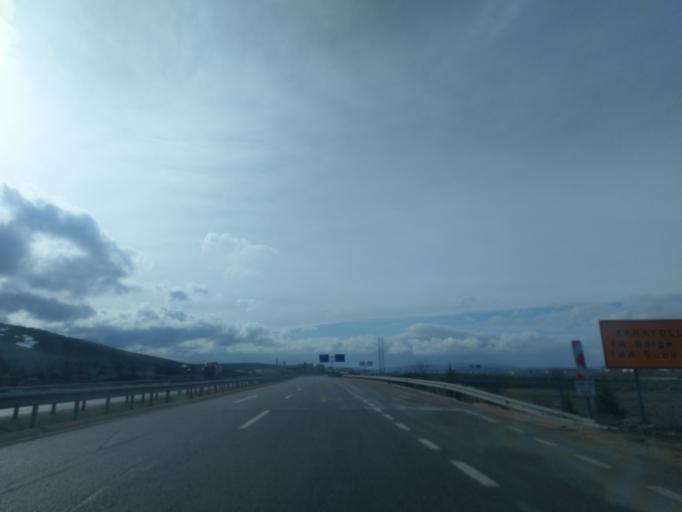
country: TR
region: Eskisehir
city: Inonu
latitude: 39.7091
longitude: 30.1624
